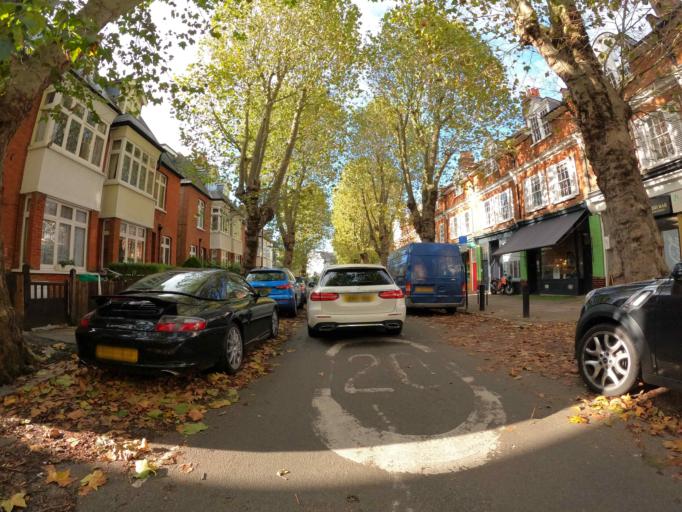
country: GB
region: England
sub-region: Greater London
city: Acton
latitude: 51.4863
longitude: -0.2715
